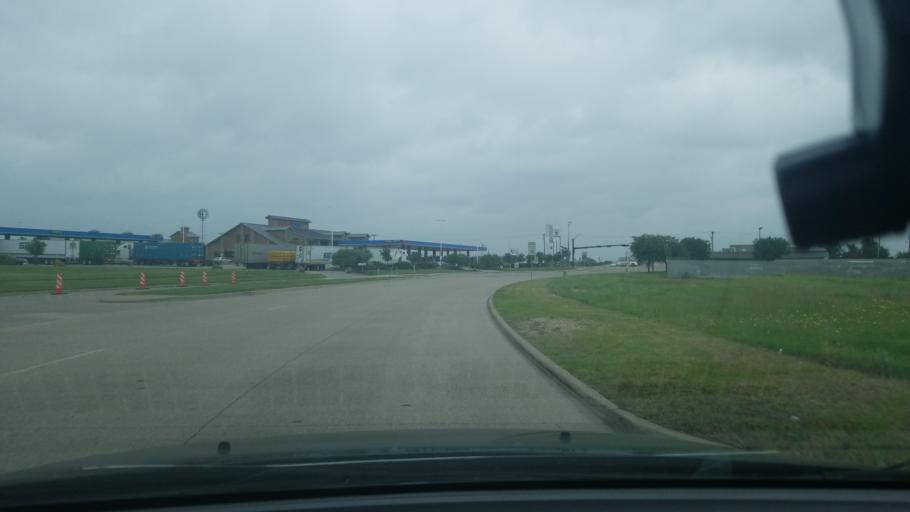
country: US
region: Texas
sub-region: Dallas County
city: Mesquite
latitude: 32.7899
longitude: -96.6555
